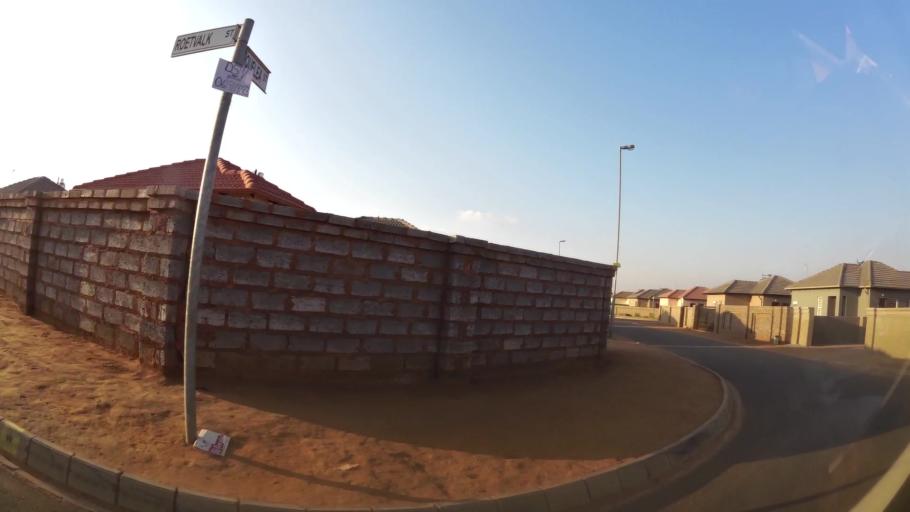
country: ZA
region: Gauteng
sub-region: Ekurhuleni Metropolitan Municipality
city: Benoni
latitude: -26.1401
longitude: 28.3807
